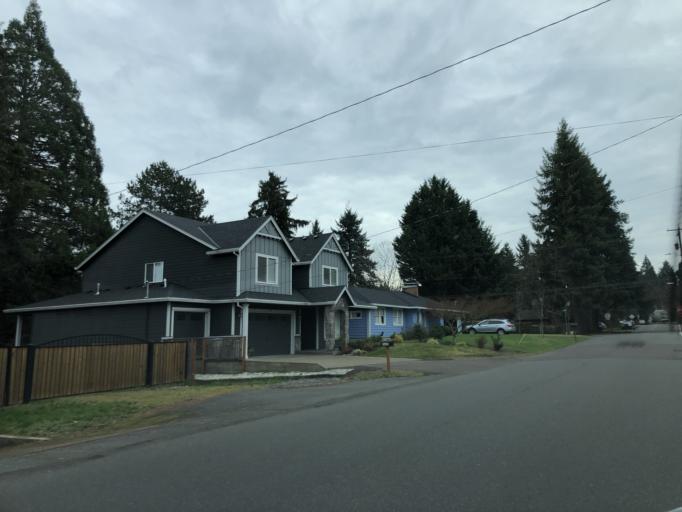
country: US
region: Oregon
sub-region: Washington County
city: Tigard
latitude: 45.4236
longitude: -122.7770
